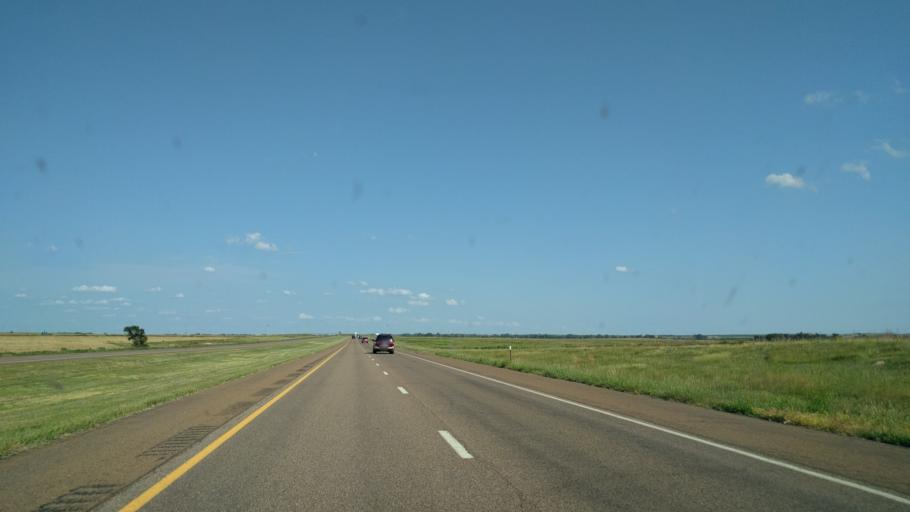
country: US
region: Kansas
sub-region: Ellis County
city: Ellis
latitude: 38.9555
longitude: -99.6125
